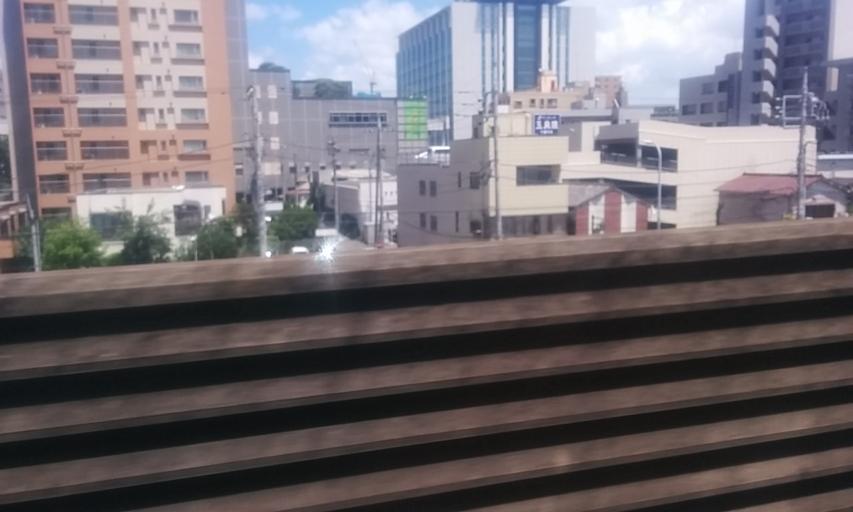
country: JP
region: Chiba
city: Chiba
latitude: 35.6030
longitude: 140.1202
